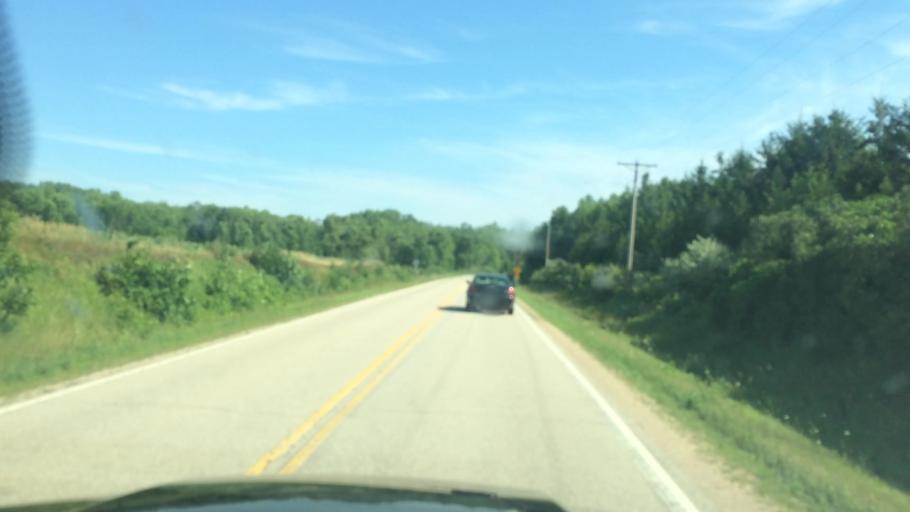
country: US
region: Wisconsin
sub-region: Oconto County
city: Gillett
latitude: 44.7903
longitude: -88.3119
